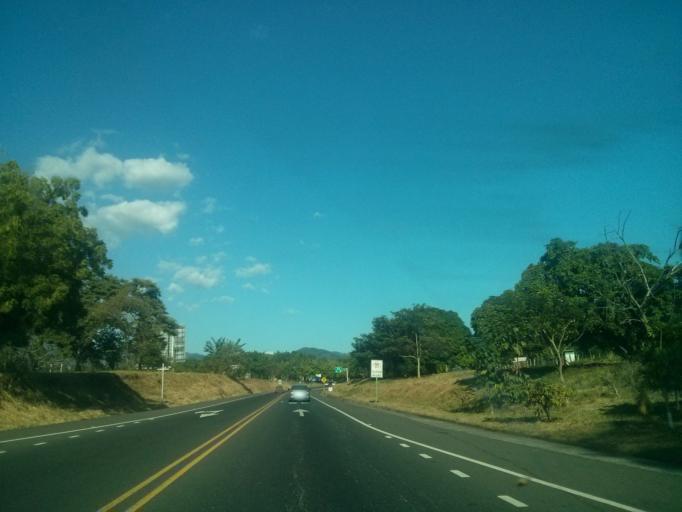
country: CR
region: Alajuela
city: Orotina
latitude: 9.9037
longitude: -84.5280
